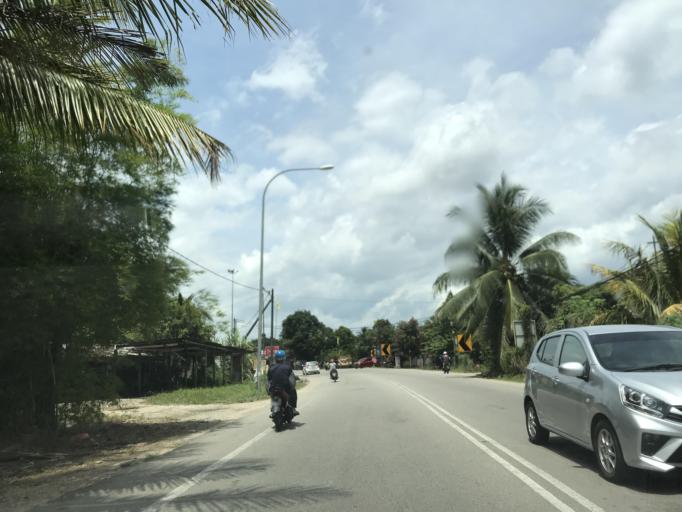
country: MY
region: Kelantan
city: Kota Bharu
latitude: 6.0832
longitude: 102.2071
